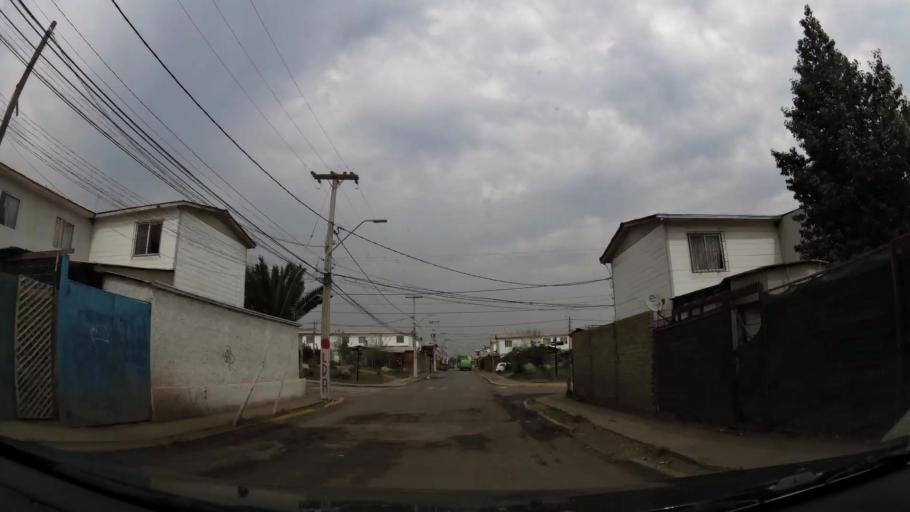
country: CL
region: Santiago Metropolitan
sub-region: Provincia de Chacabuco
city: Chicureo Abajo
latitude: -33.1847
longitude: -70.6639
